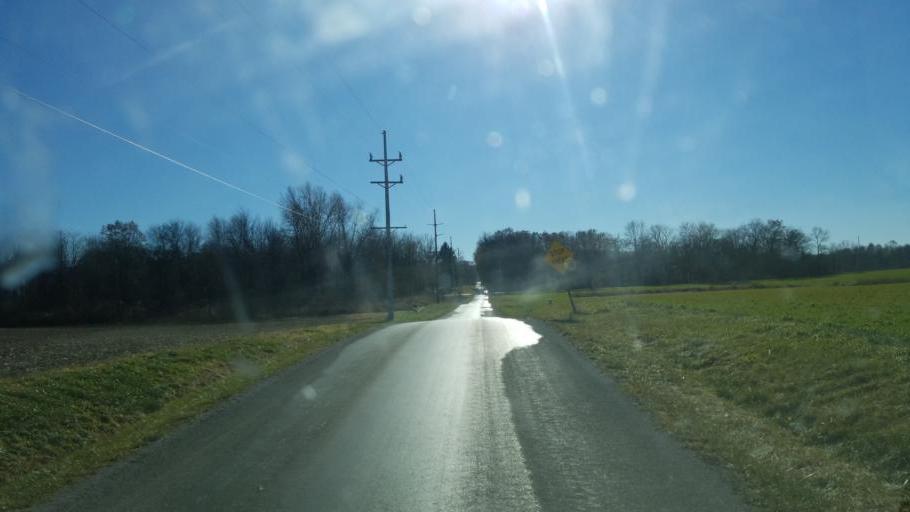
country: US
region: Ohio
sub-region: Huron County
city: Plymouth
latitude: 40.9620
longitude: -82.6958
